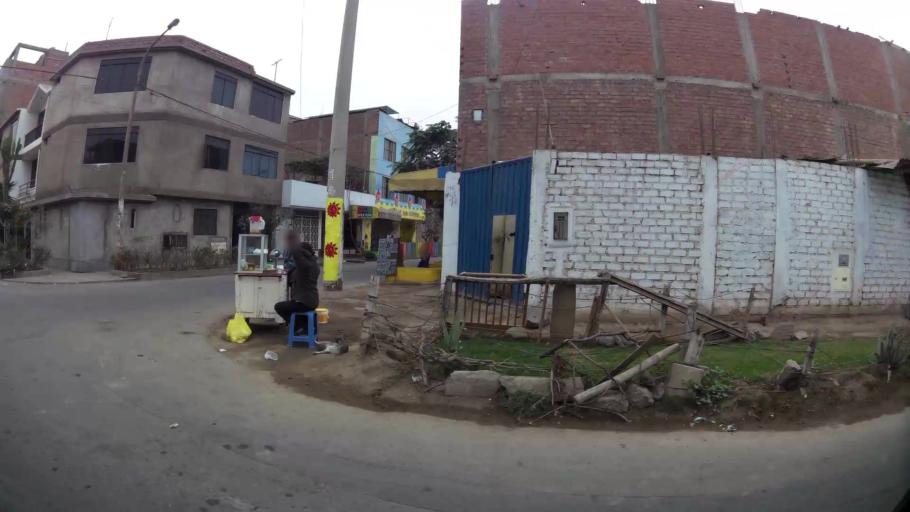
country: PE
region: Lima
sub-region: Lima
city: Independencia
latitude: -11.9592
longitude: -77.0775
